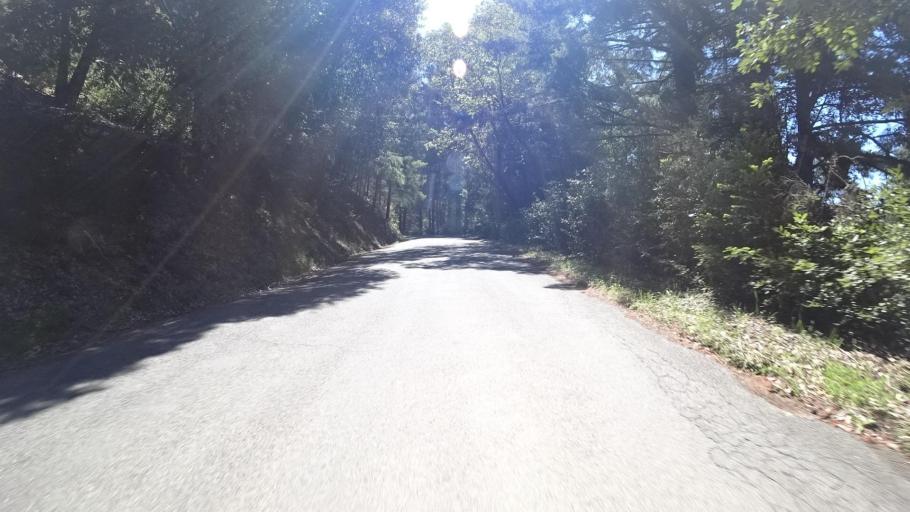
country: US
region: California
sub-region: Humboldt County
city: Redway
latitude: 40.1141
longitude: -123.9649
